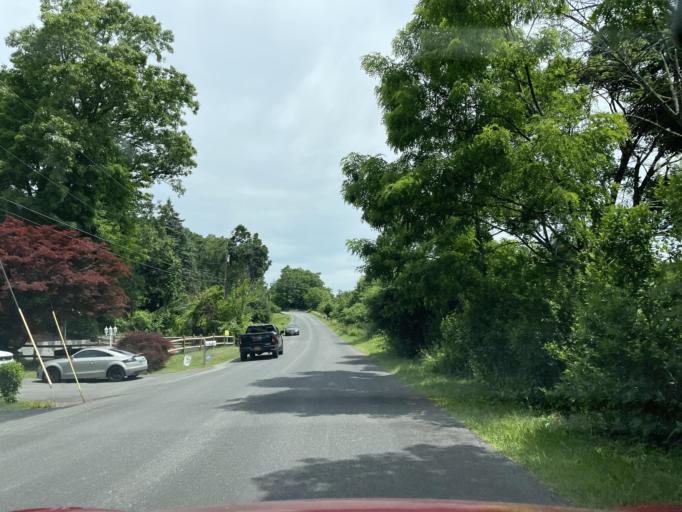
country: US
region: New York
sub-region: Ulster County
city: Lincoln Park
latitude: 41.9561
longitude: -74.0270
